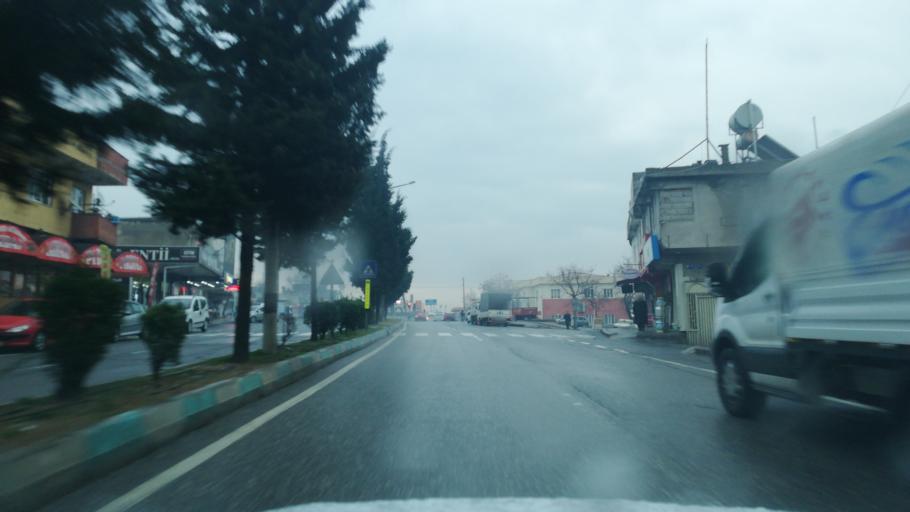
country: TR
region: Kahramanmaras
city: Kahramanmaras
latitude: 37.5817
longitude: 36.9438
